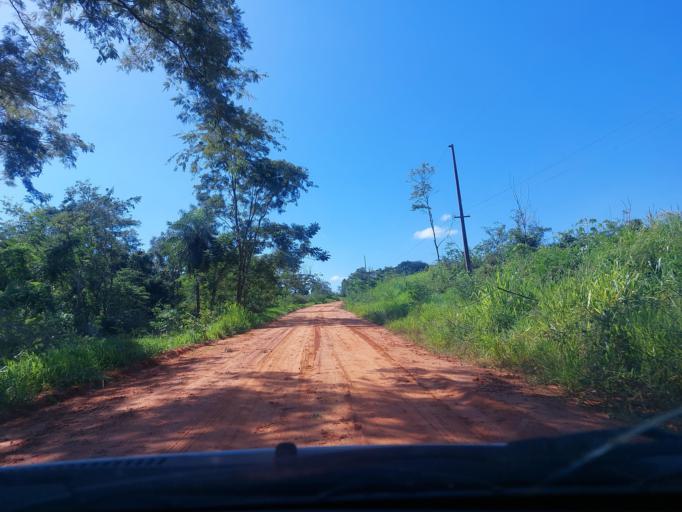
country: PY
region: San Pedro
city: Itacurubi del Rosario
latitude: -24.5431
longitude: -56.5841
